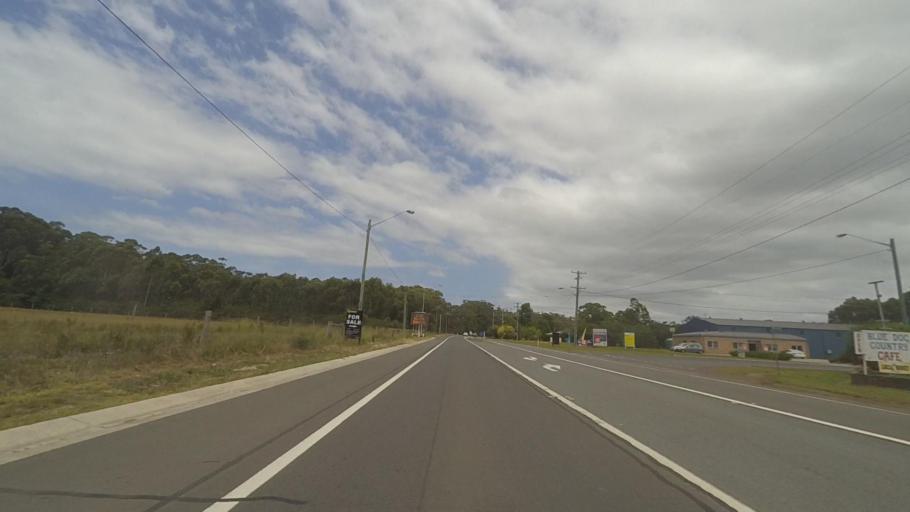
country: AU
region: New South Wales
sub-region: Shoalhaven Shire
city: Falls Creek
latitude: -35.0933
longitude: 150.5069
